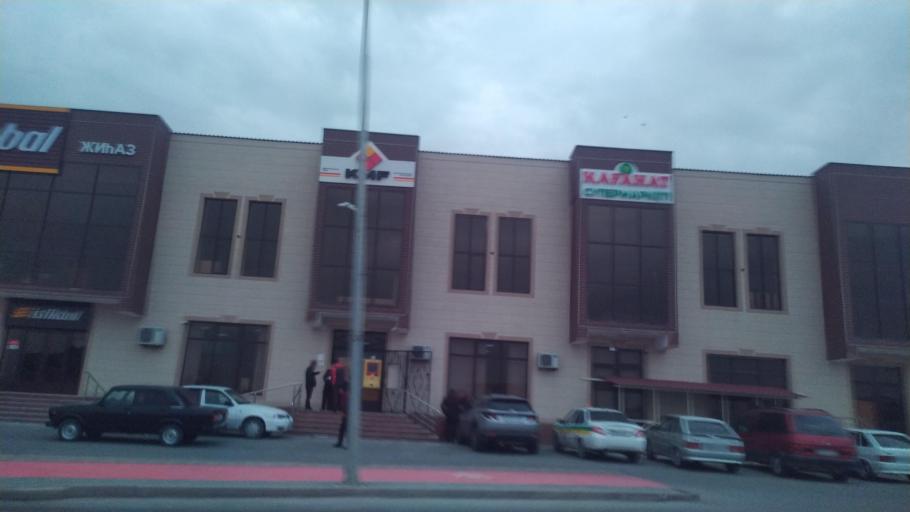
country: KZ
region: Ongtustik Qazaqstan
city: Turkestan
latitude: 43.2816
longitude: 68.3176
